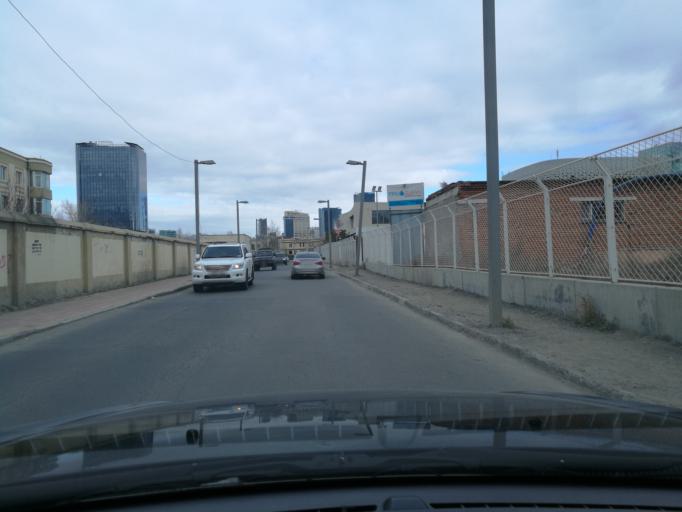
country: MN
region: Ulaanbaatar
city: Ulaanbaatar
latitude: 47.9025
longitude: 106.9207
